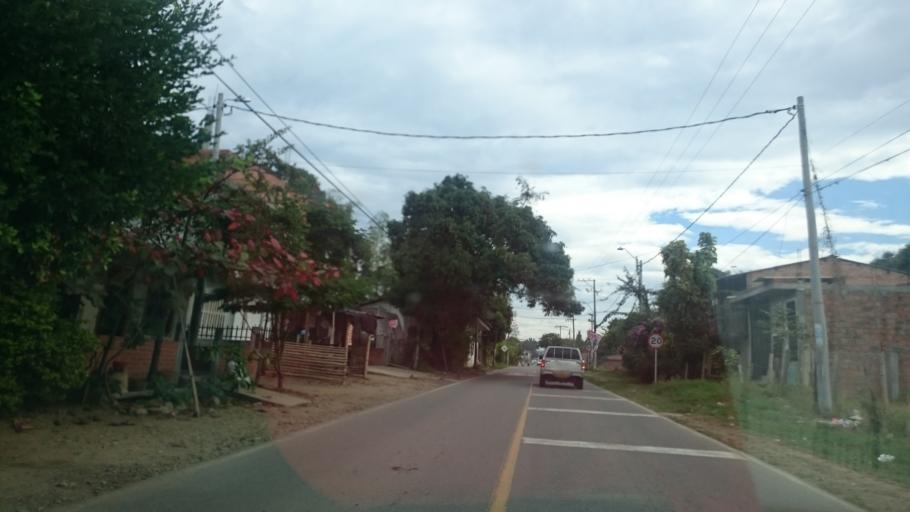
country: CO
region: Cauca
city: Santander de Quilichao
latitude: 3.0230
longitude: -76.4783
